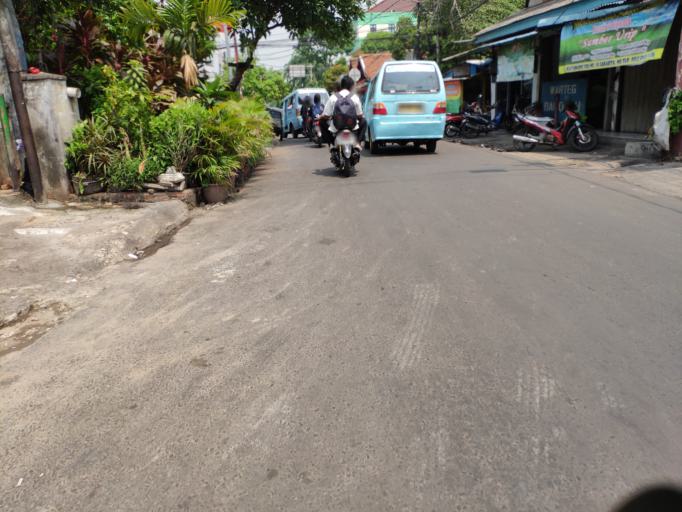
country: ID
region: Jakarta Raya
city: Jakarta
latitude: -6.2062
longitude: 106.8650
